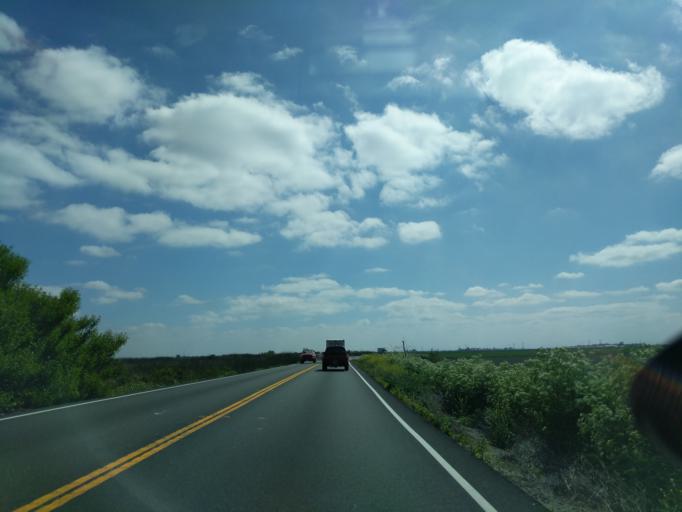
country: US
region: California
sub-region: Contra Costa County
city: Discovery Bay
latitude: 37.8966
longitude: -121.4811
